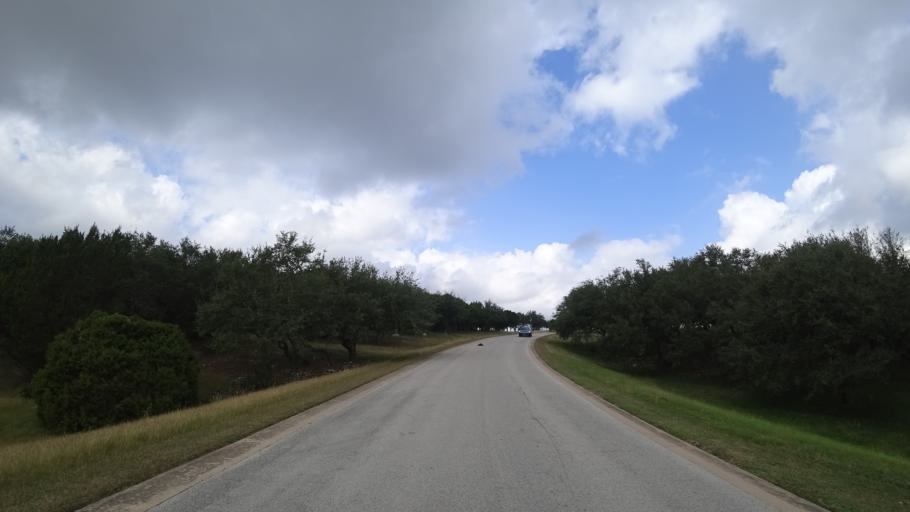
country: US
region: Texas
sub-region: Travis County
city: Barton Creek
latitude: 30.3039
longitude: -97.8929
